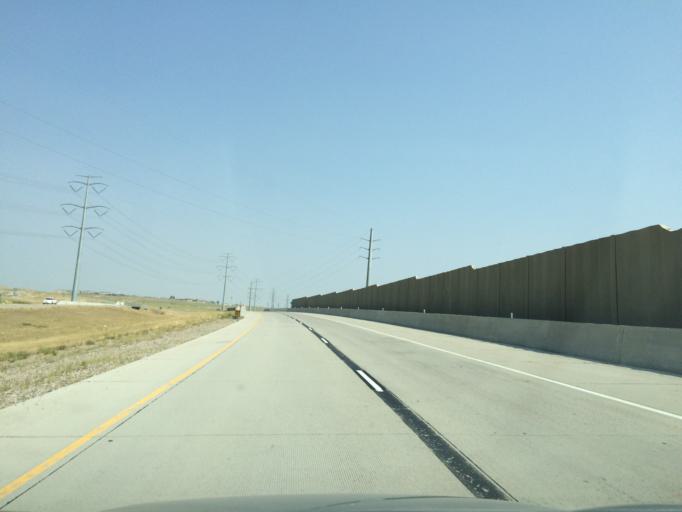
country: US
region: Utah
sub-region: Salt Lake County
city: Oquirrh
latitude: 40.6003
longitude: -112.0291
